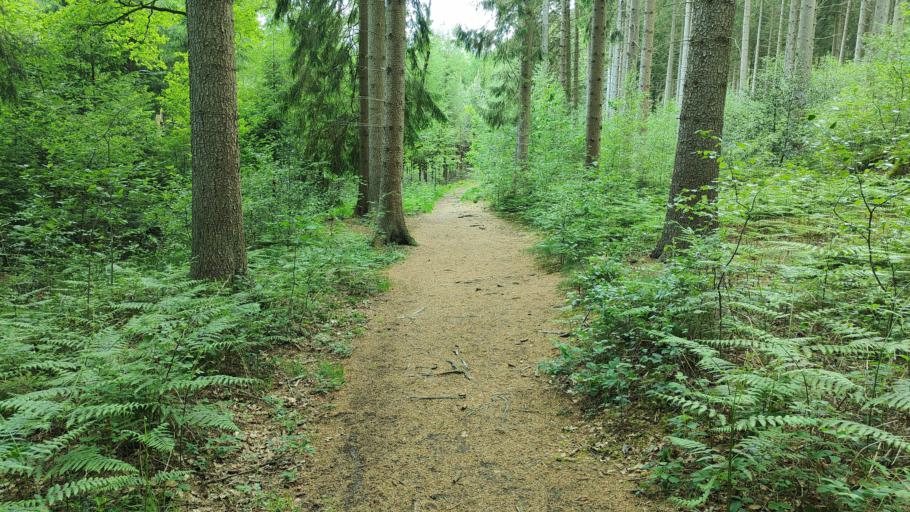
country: BE
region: Wallonia
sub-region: Province de Liege
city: La Calamine
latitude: 50.7155
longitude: 6.0586
